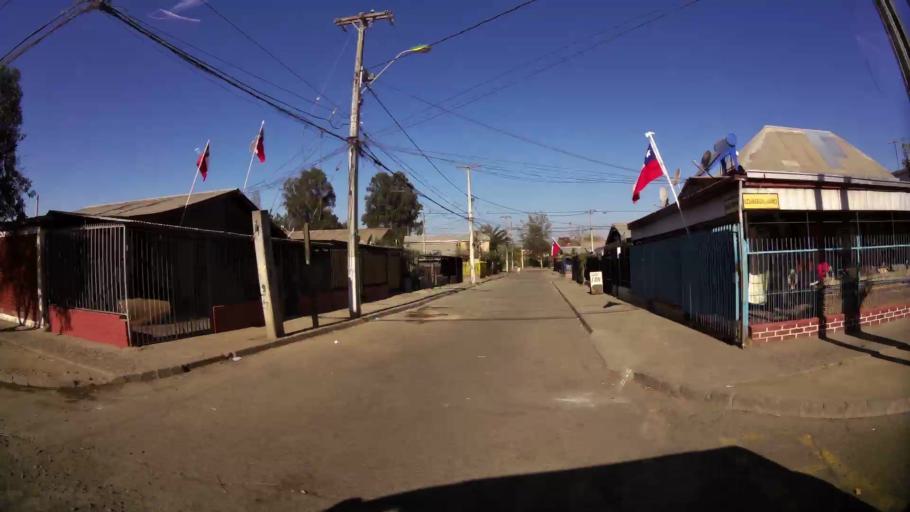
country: CL
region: Santiago Metropolitan
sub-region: Provincia de Talagante
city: Penaflor
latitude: -33.6062
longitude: -70.8684
